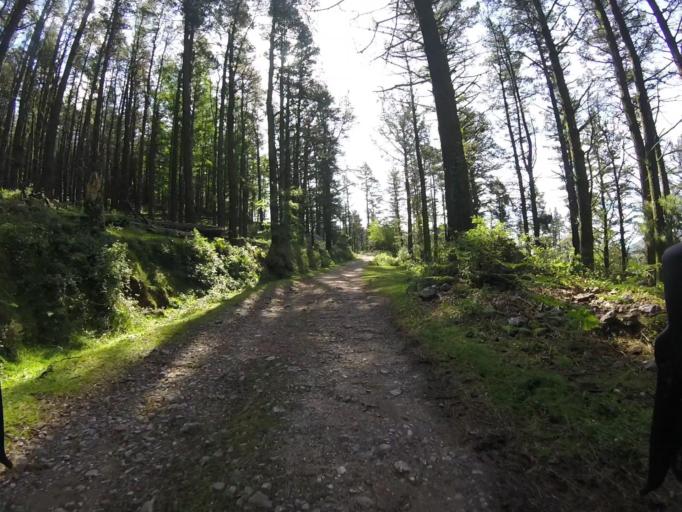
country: ES
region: Basque Country
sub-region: Provincia de Guipuzcoa
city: Andoain
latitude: 43.1944
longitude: -1.9915
